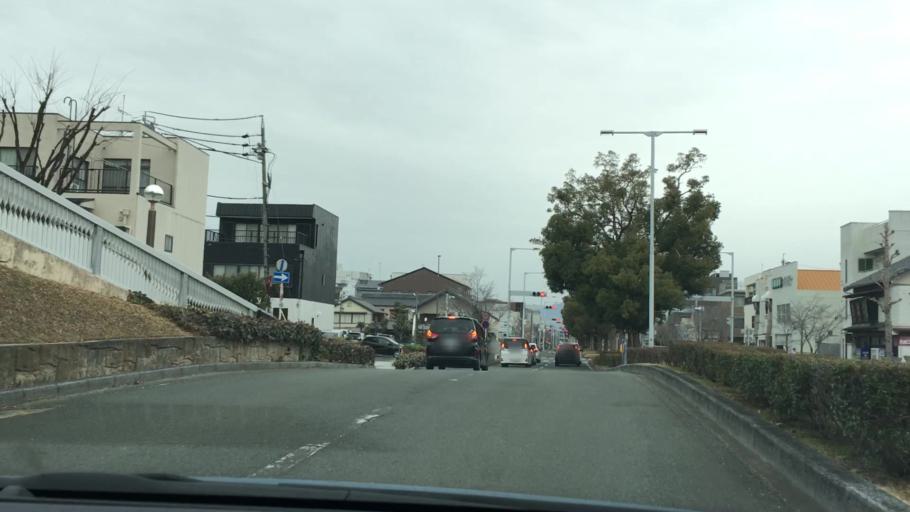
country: JP
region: Aichi
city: Toyohashi
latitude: 34.7627
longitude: 137.3945
